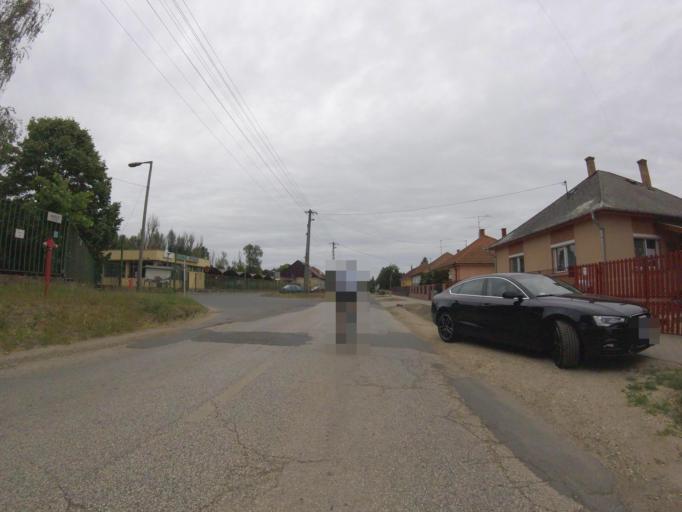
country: HU
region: Pest
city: Dabas
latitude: 47.1788
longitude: 19.3460
